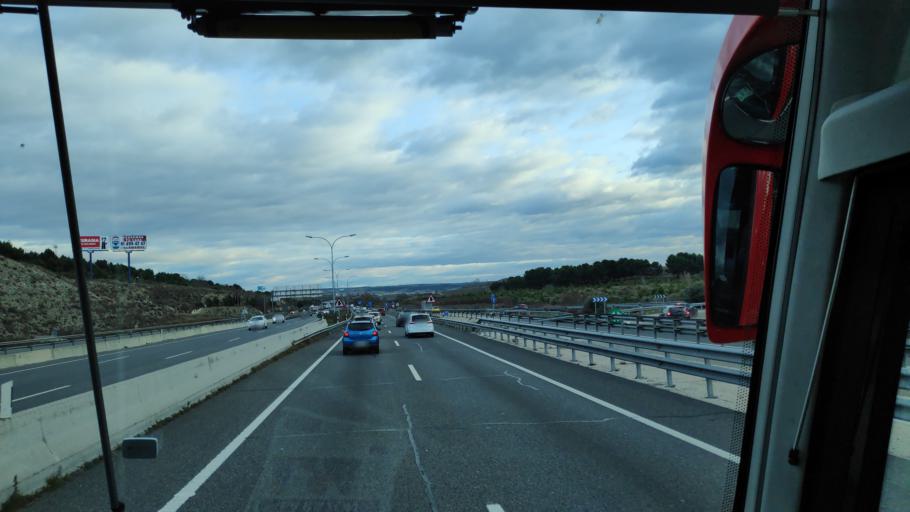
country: ES
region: Madrid
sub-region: Provincia de Madrid
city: Vaciamadrid
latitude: 40.3526
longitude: -3.5510
